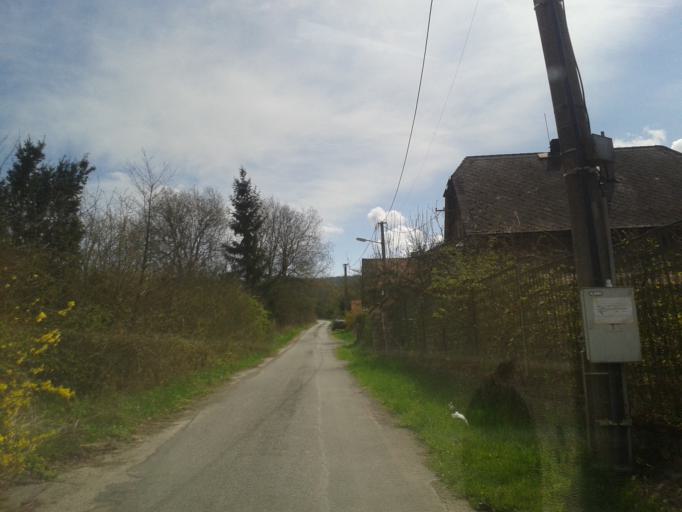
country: CZ
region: Central Bohemia
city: Dobris
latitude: 49.8684
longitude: 14.1421
